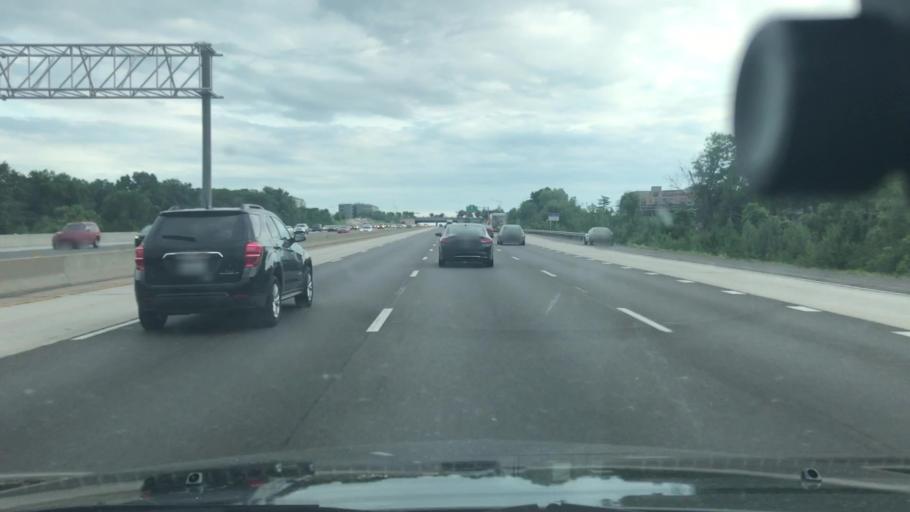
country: US
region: Missouri
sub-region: Saint Louis County
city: Creve Coeur
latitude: 38.6797
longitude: -90.4498
